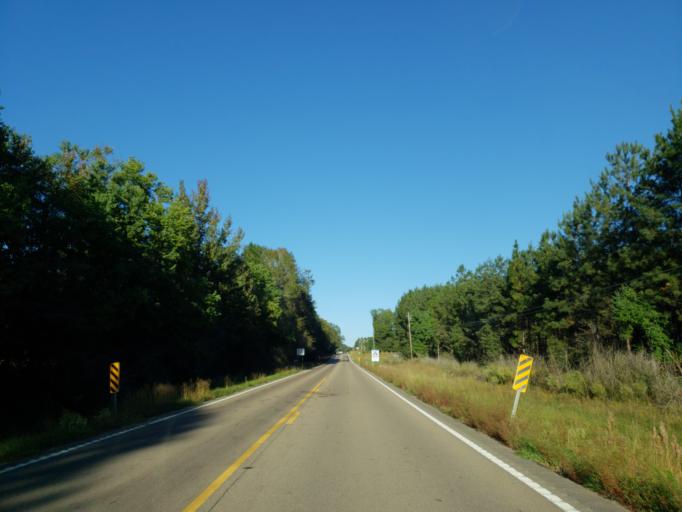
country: US
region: Mississippi
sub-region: Perry County
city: Richton
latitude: 31.3697
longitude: -88.8720
